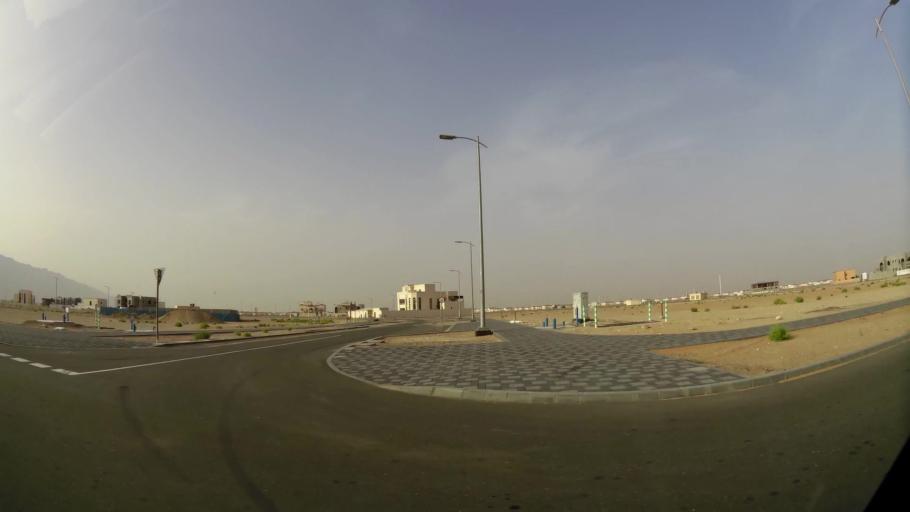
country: AE
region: Abu Dhabi
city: Al Ain
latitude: 24.1039
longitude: 55.7025
